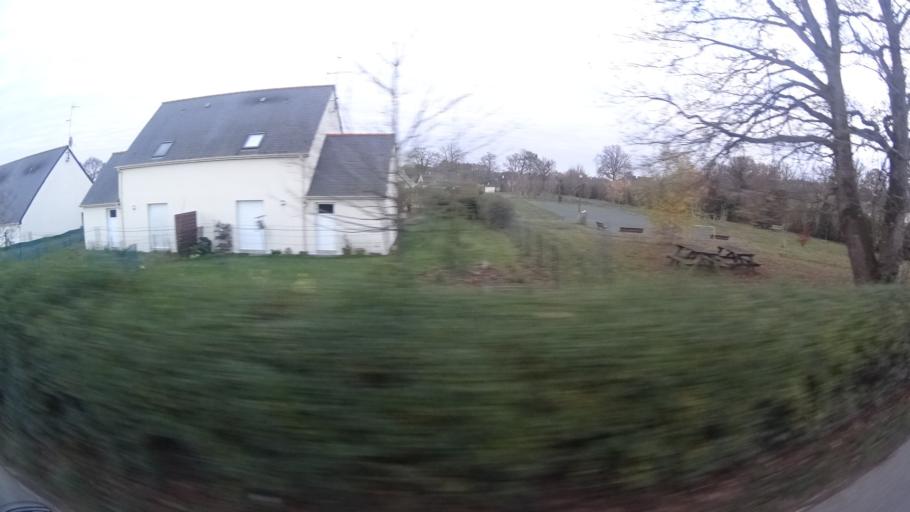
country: FR
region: Pays de la Loire
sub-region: Departement de la Loire-Atlantique
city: Avessac
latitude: 47.6486
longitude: -1.9964
